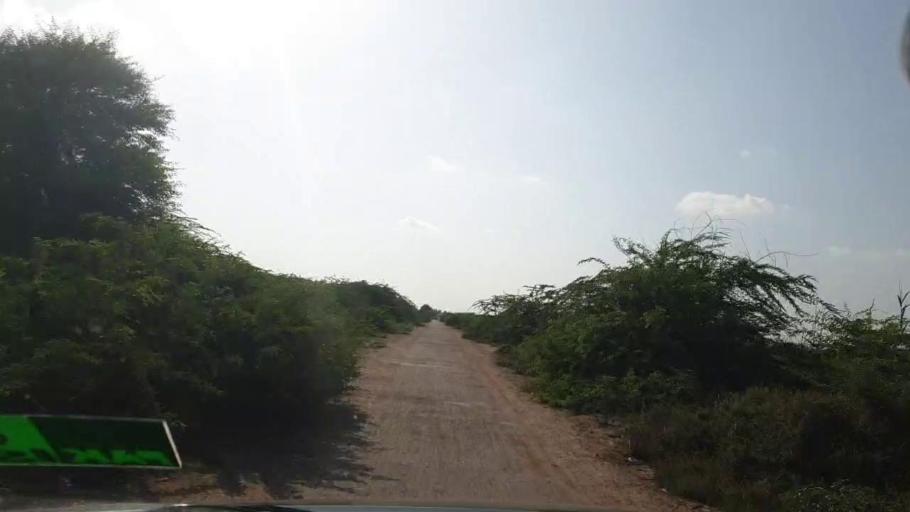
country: PK
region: Sindh
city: Tando Bago
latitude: 24.7117
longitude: 69.2007
